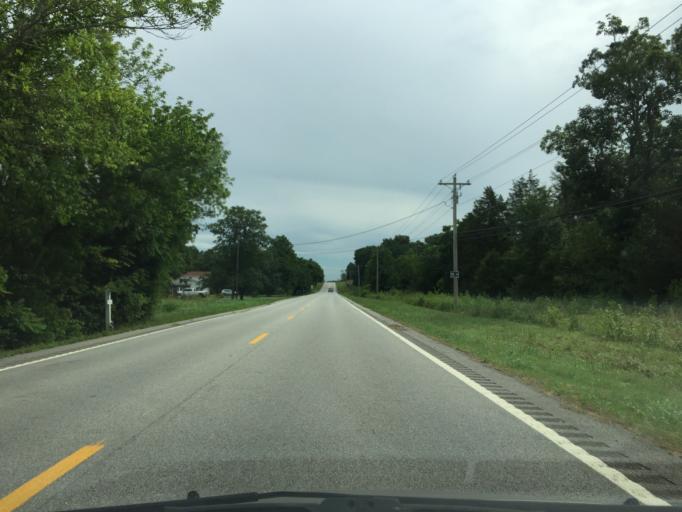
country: US
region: Tennessee
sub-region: Bradley County
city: Hopewell
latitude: 35.2930
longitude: -84.9662
